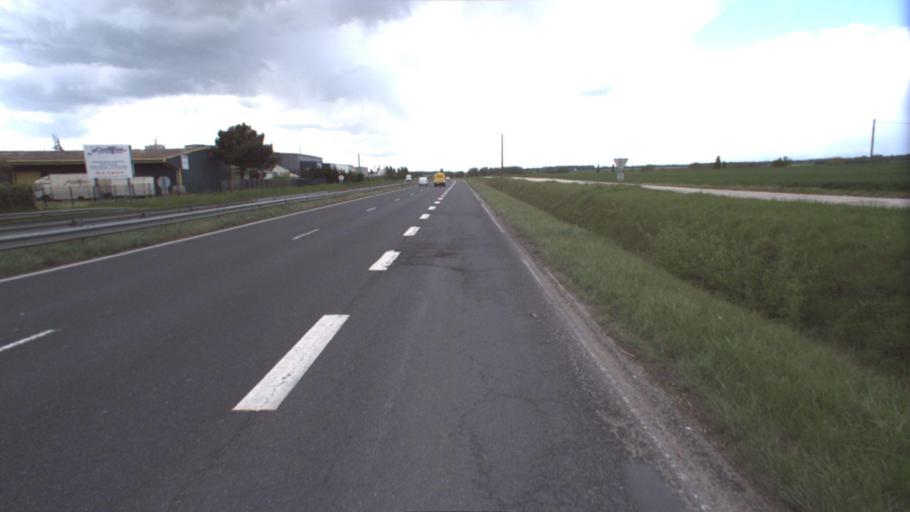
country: FR
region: Ile-de-France
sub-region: Departement de Seine-et-Marne
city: Rozay-en-Brie
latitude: 48.6876
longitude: 2.9647
